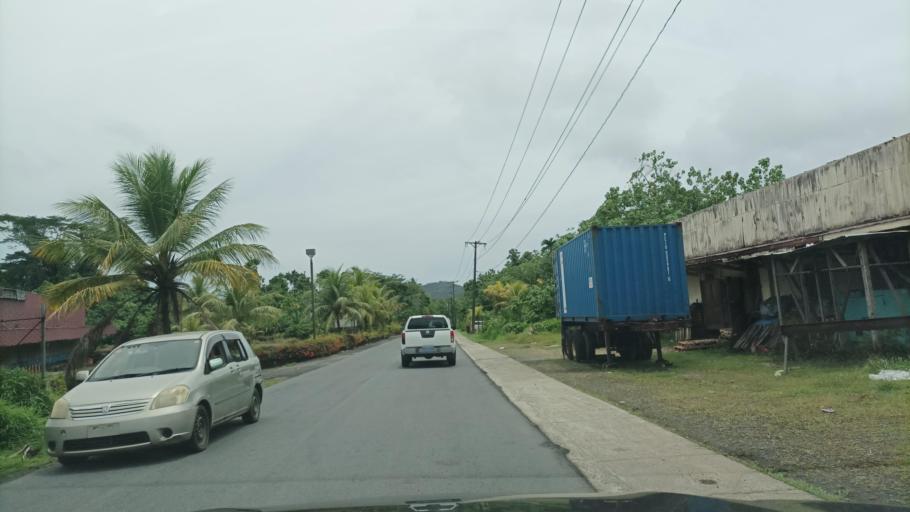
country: FM
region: Pohnpei
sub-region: Sokehs Municipality
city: Palikir - National Government Center
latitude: 6.9403
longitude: 158.1842
